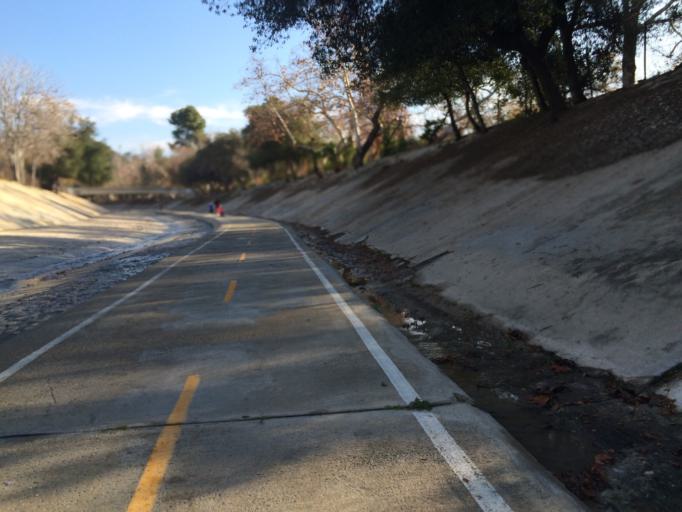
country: US
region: California
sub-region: Los Angeles County
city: South Pasadena
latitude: 34.1046
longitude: -118.1891
